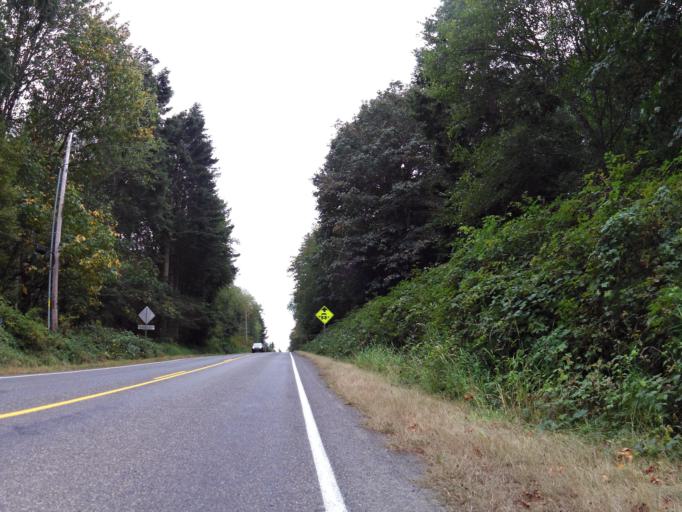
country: US
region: Washington
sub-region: Kitsap County
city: Lofall
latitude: 47.8749
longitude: -122.6362
